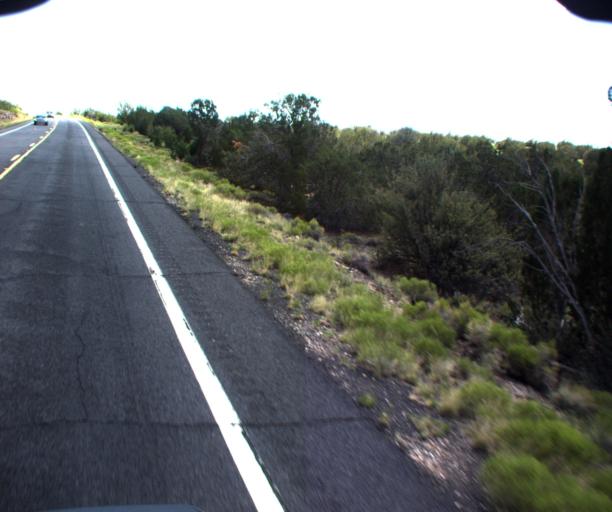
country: US
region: Arizona
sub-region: Coconino County
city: Williams
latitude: 35.5119
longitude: -112.1723
